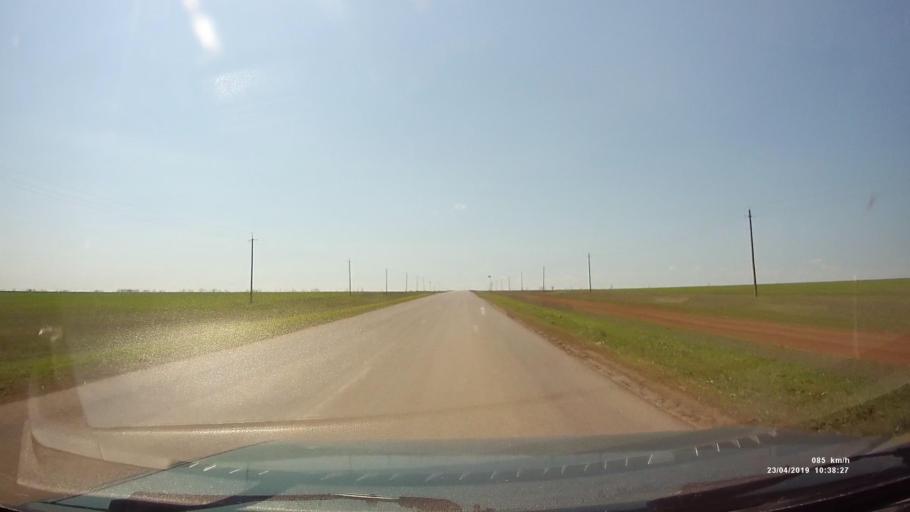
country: RU
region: Kalmykiya
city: Yashalta
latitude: 46.5324
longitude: 42.6388
